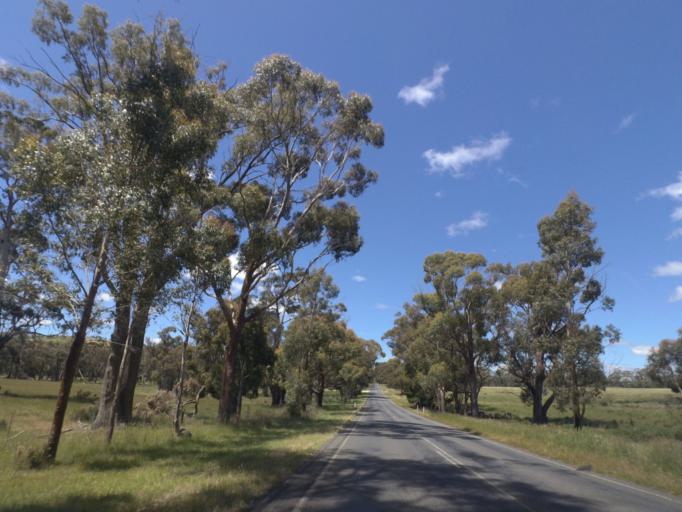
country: AU
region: Victoria
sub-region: Mount Alexander
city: Castlemaine
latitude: -37.3178
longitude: 144.2140
